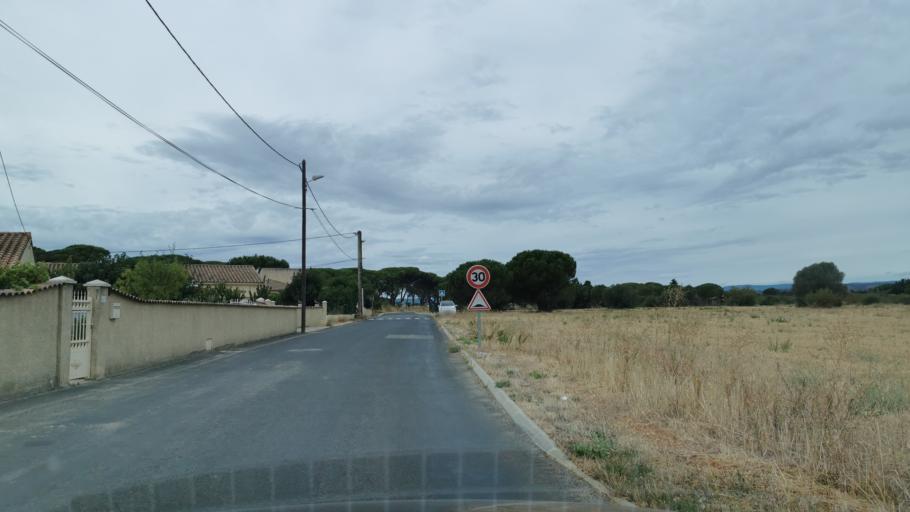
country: FR
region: Languedoc-Roussillon
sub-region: Departement de l'Aude
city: Saint-Marcel-sur-Aude
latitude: 43.2660
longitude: 2.9431
